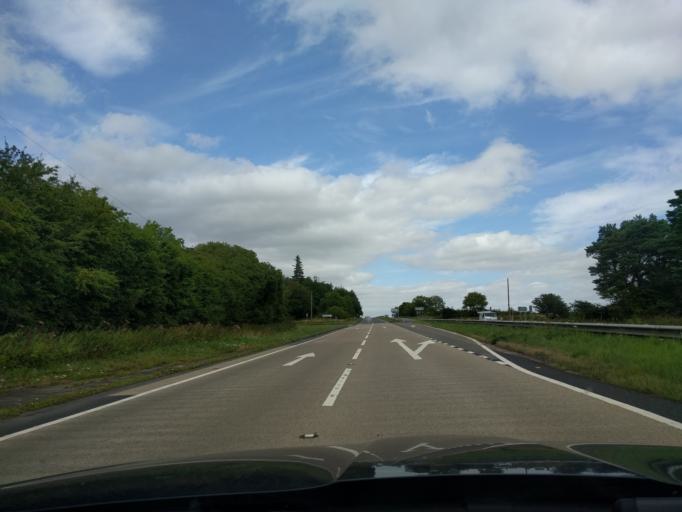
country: GB
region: England
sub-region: Northumberland
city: Felton
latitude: 55.3294
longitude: -1.7249
